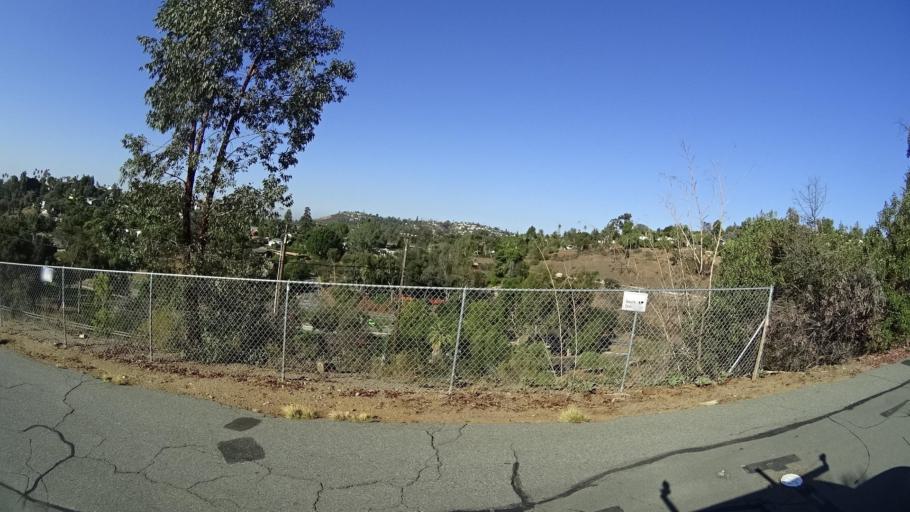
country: US
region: California
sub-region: San Diego County
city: Spring Valley
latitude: 32.7605
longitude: -117.0004
